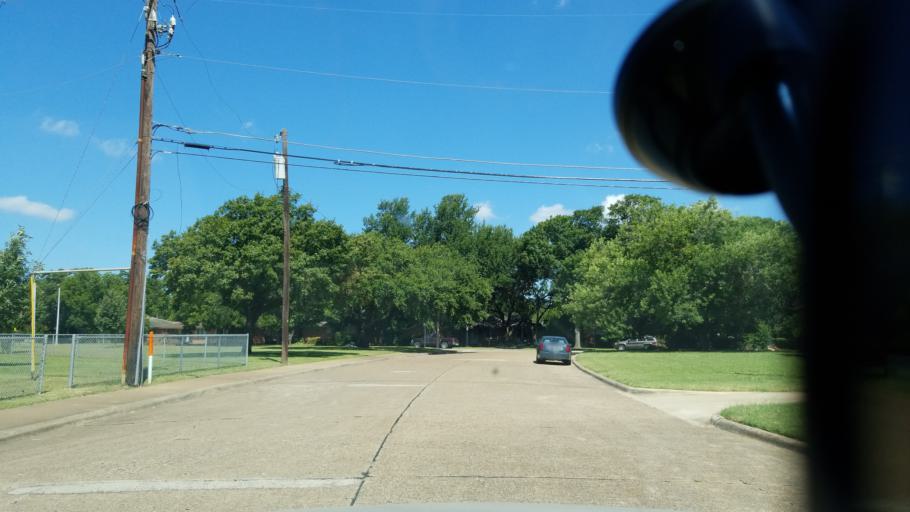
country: US
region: Texas
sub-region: Dallas County
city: Cockrell Hill
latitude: 32.6848
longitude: -96.8326
